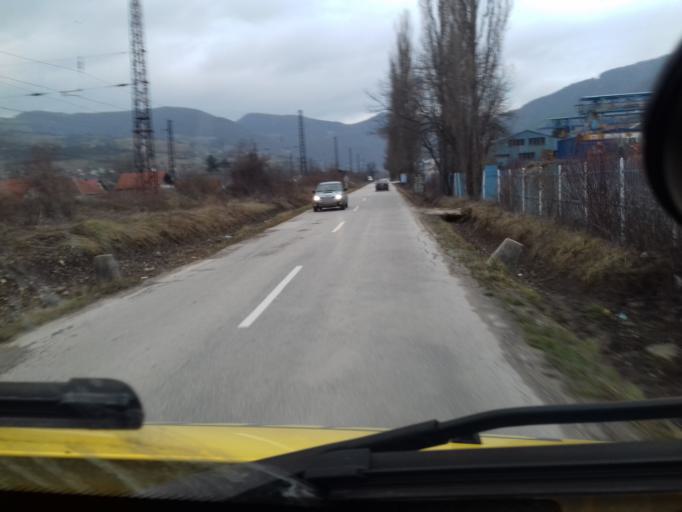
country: BA
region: Federation of Bosnia and Herzegovina
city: Zenica
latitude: 44.1733
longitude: 17.9699
